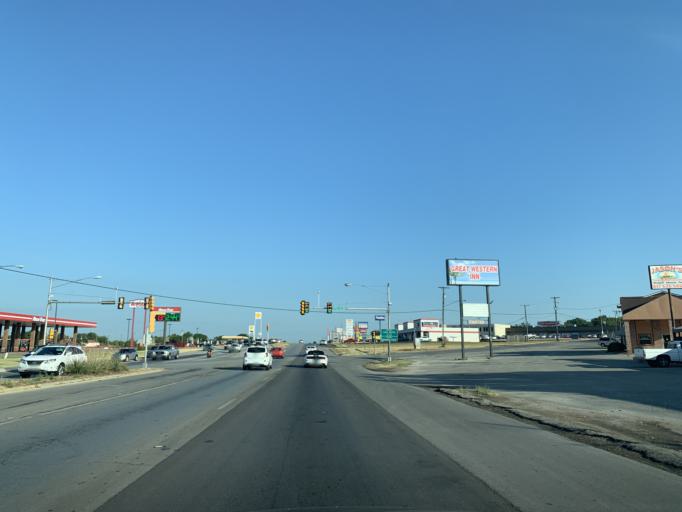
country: US
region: Texas
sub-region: Tarrant County
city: Sansom Park
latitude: 32.8037
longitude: -97.4114
